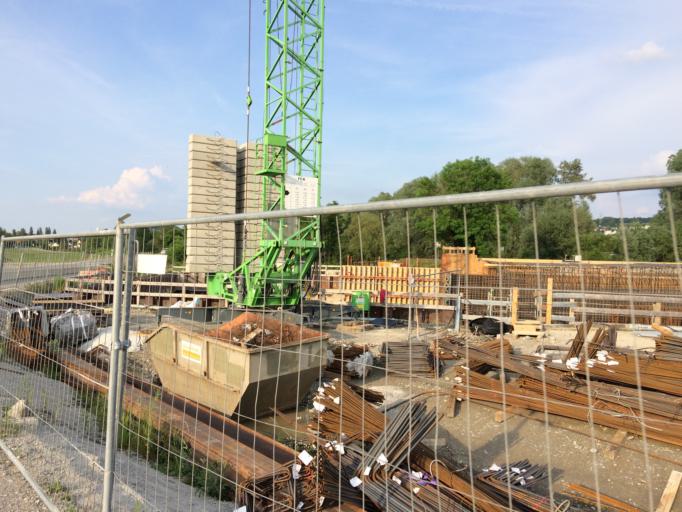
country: DE
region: Baden-Wuerttemberg
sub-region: Tuebingen Region
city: Ravensburg
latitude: 47.7619
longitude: 9.5886
